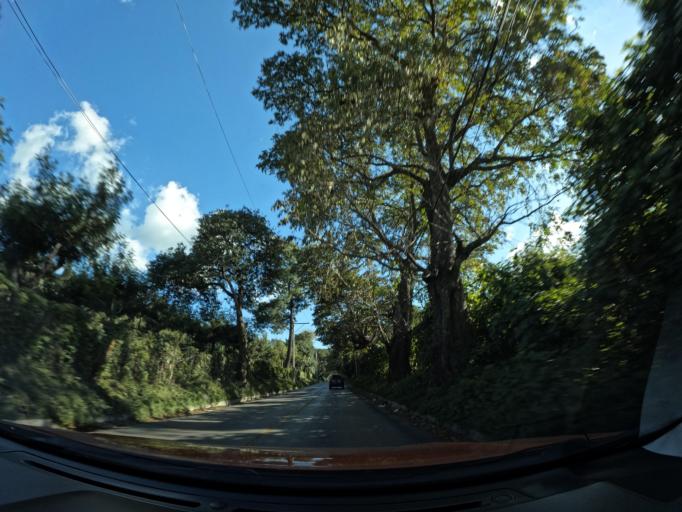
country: GT
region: Sacatepequez
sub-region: Municipio de Santa Maria de Jesus
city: Santa Maria de Jesus
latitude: 14.5281
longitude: -90.7266
